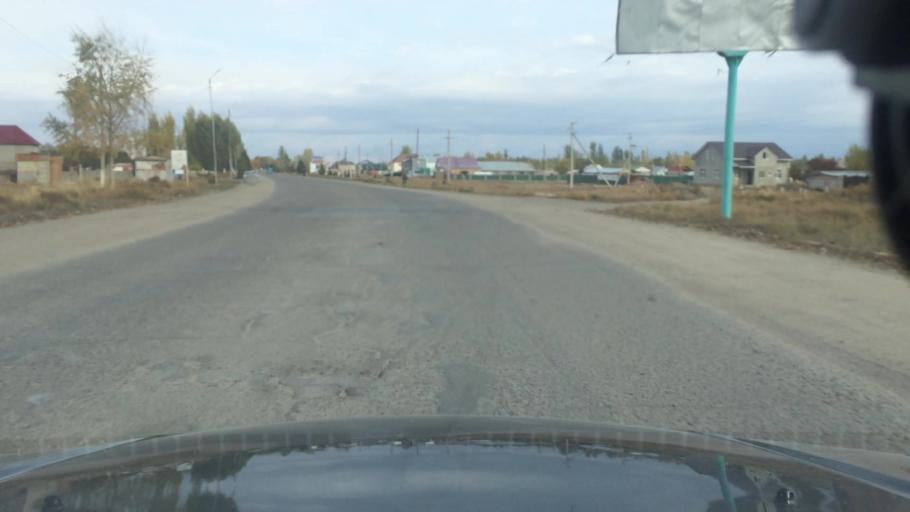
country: KG
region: Ysyk-Koel
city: Karakol
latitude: 42.5227
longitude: 78.3861
